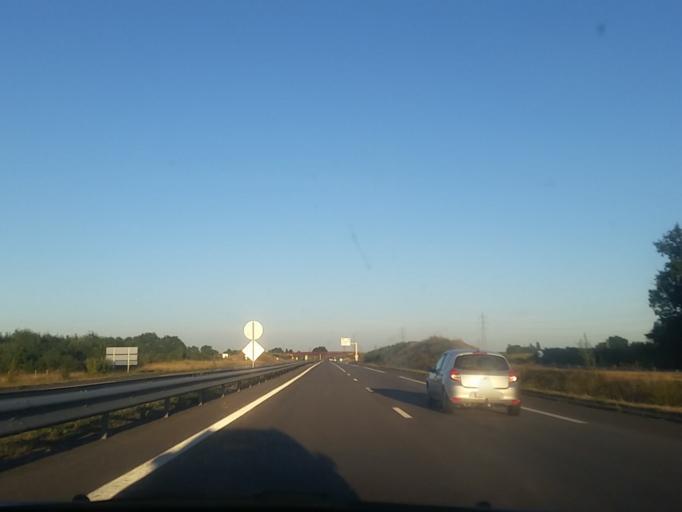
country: FR
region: Pays de la Loire
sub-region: Departement de la Loire-Atlantique
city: Brains
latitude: 47.1792
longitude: -1.7106
